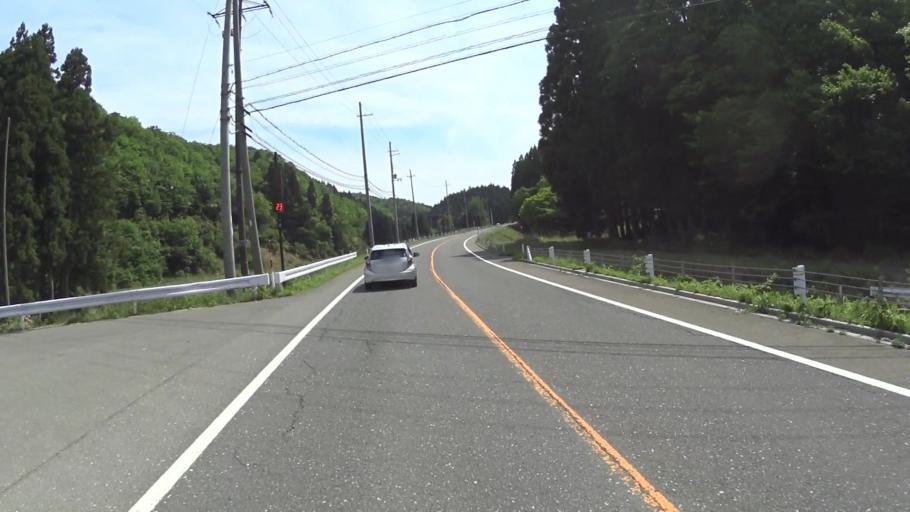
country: JP
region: Fukui
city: Obama
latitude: 35.4011
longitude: 135.9336
